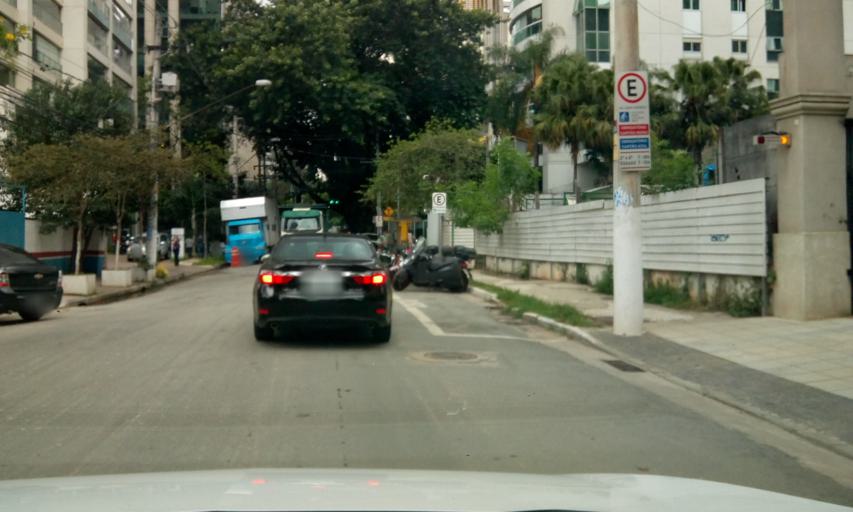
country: BR
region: Sao Paulo
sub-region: Sao Paulo
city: Sao Paulo
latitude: -23.5893
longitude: -46.6839
